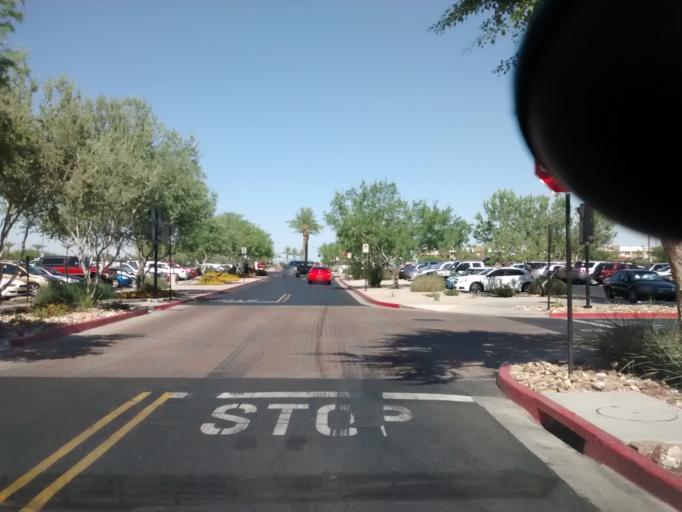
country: US
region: Arizona
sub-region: Maricopa County
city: Peoria
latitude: 33.5350
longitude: -112.2608
